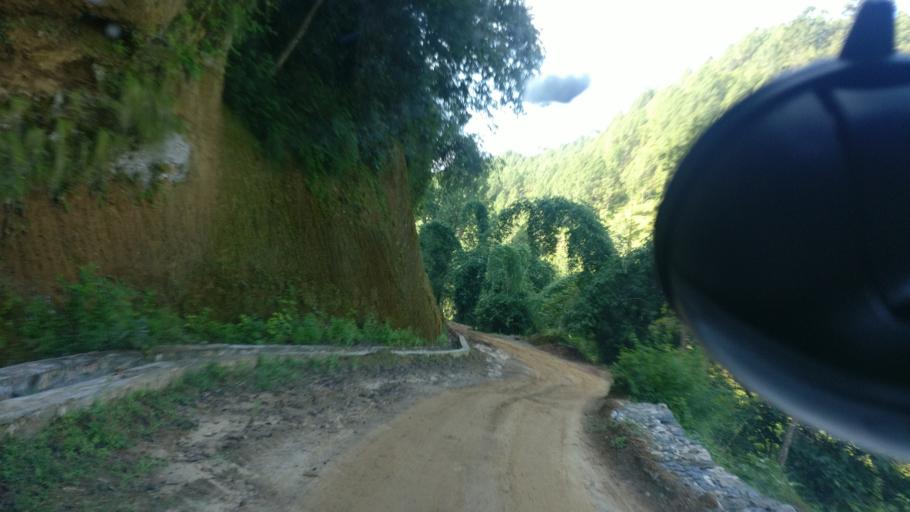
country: NP
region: Western Region
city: Baglung
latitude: 28.1608
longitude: 83.6545
